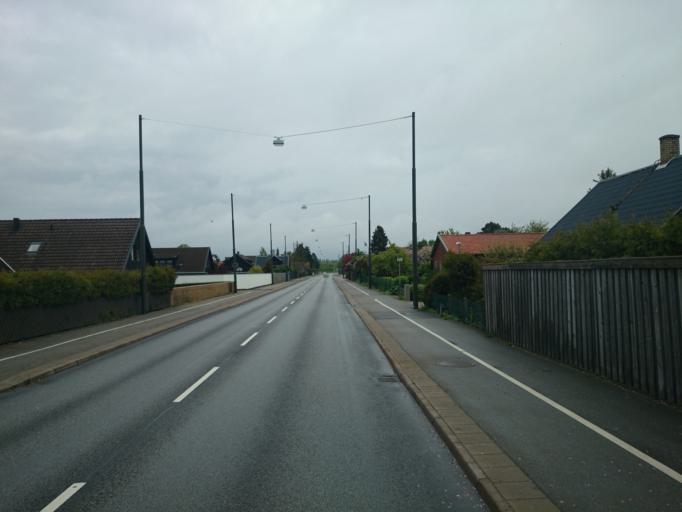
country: SE
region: Skane
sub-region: Malmo
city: Bunkeflostrand
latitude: 55.5587
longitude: 12.9191
